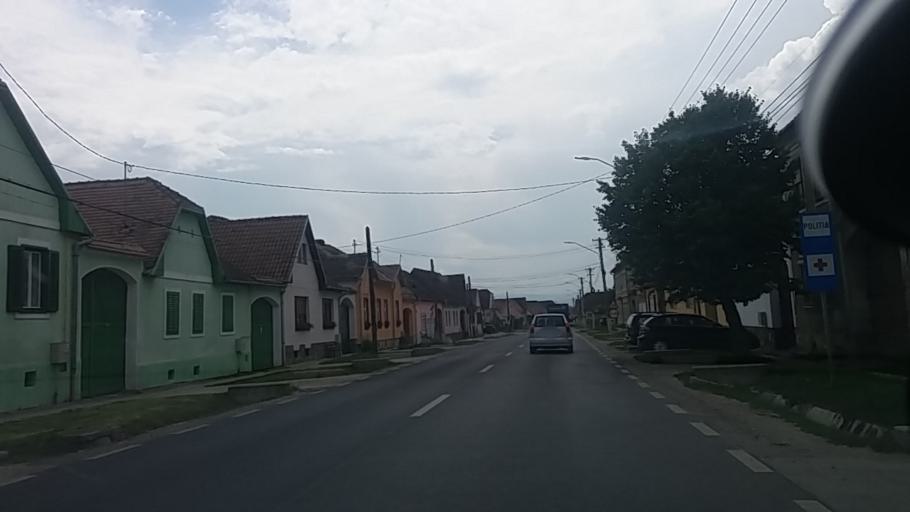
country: RO
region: Sibiu
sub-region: Comuna Sura Mare
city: Sura Mare
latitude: 45.8531
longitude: 24.1676
